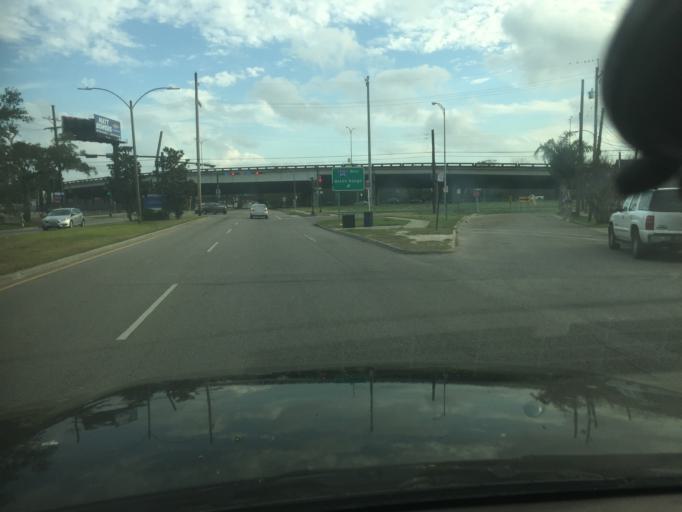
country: US
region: Louisiana
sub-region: Orleans Parish
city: New Orleans
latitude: 29.9943
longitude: -90.0781
